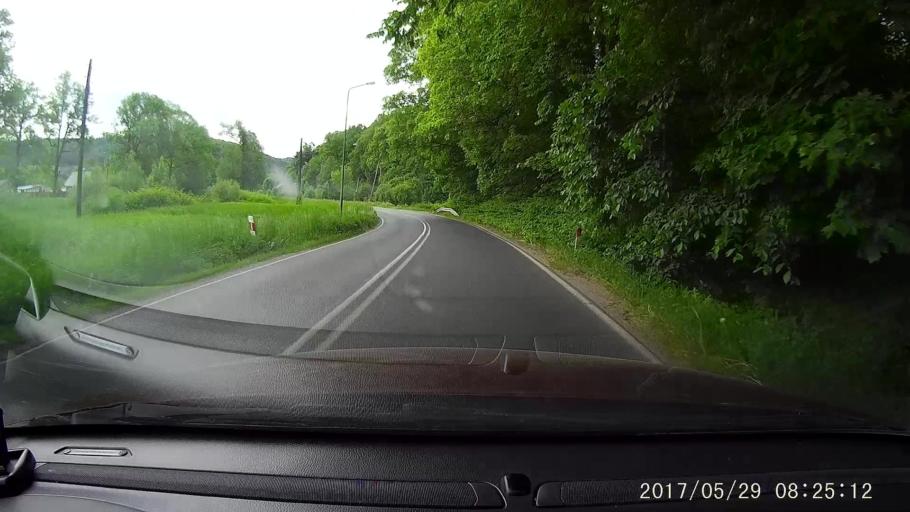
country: PL
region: Lower Silesian Voivodeship
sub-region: Powiat zlotoryjski
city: Swierzawa
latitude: 51.0671
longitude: 15.8642
